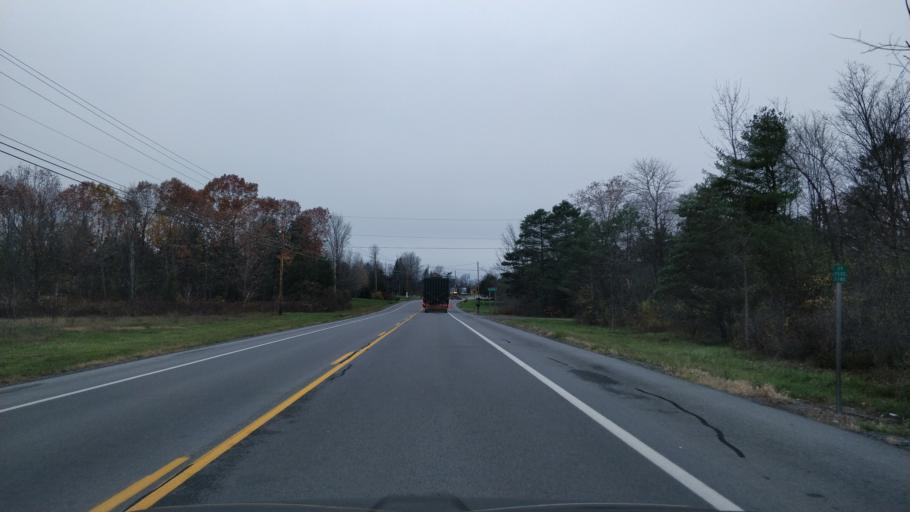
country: CA
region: Ontario
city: Brockville
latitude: 44.5982
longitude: -75.6286
